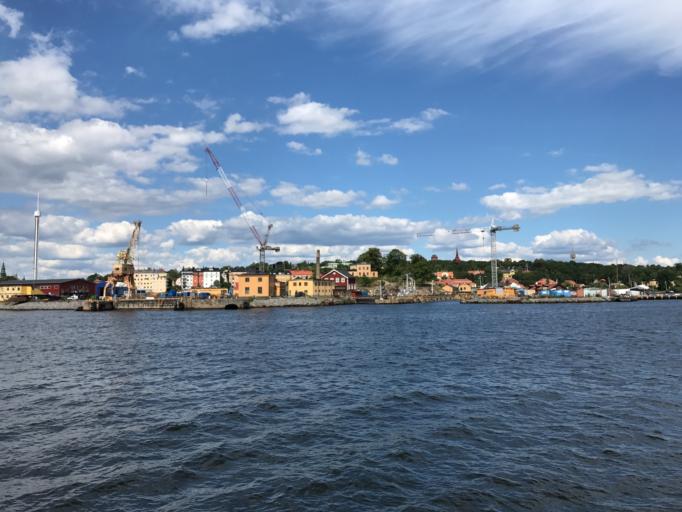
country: SE
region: Stockholm
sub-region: Stockholms Kommun
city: OEstermalm
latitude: 59.3181
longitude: 18.0988
